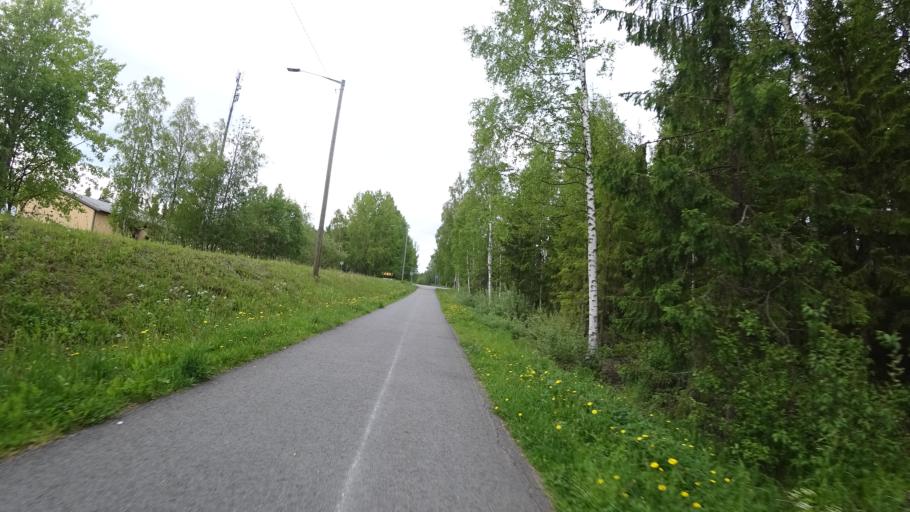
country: FI
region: Pirkanmaa
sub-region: Tampere
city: Yloejaervi
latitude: 61.5178
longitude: 23.5963
